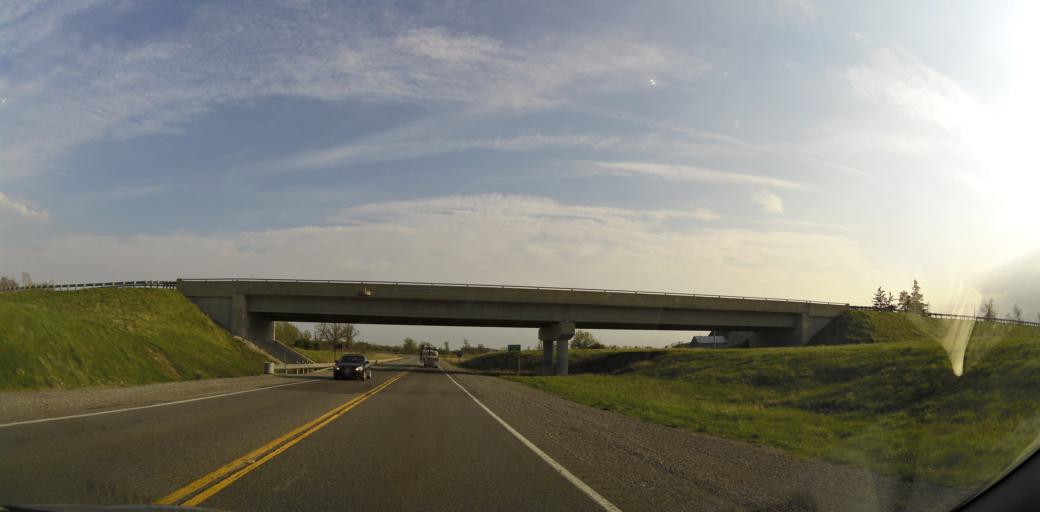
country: CA
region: Ontario
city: Ancaster
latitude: 43.1477
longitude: -79.9271
